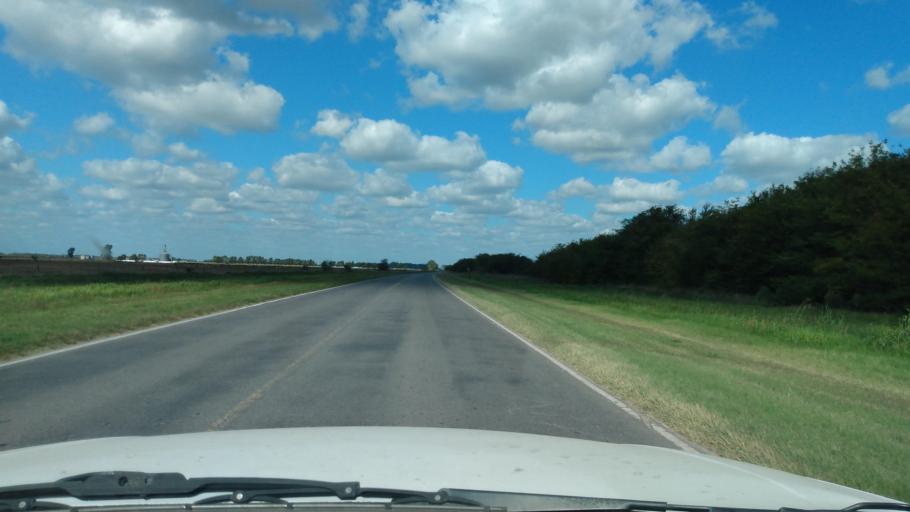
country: AR
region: Buenos Aires
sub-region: Partido de Navarro
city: Navarro
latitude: -34.9599
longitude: -59.3186
